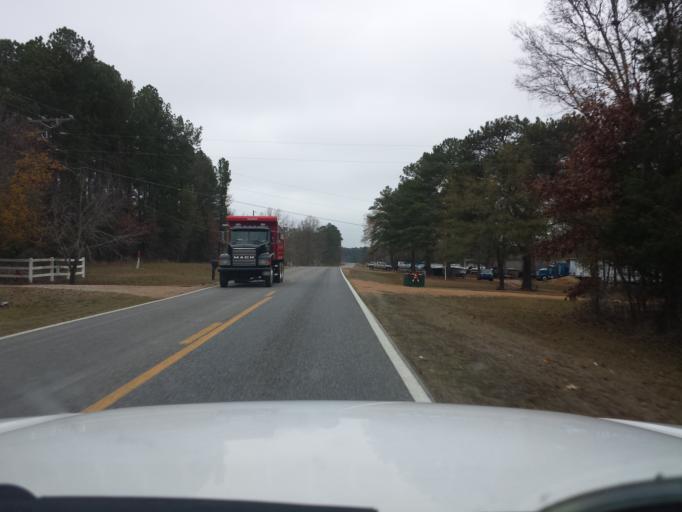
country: US
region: Mississippi
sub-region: Madison County
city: Canton
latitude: 32.4893
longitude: -89.9217
